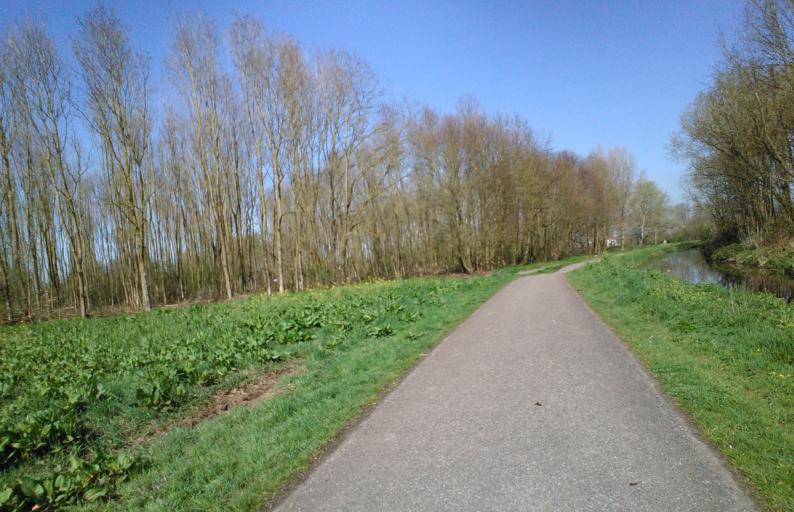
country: NL
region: South Holland
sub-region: Gemeente Krimpen aan den IJssel
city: Krimpen aan den IJssel
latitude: 51.9636
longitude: 4.6305
